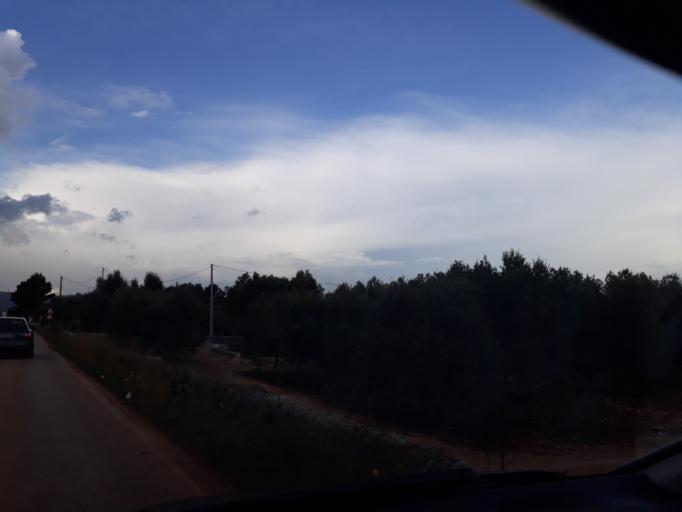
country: IT
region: Apulia
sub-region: Provincia di Brindisi
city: Pezze di Greco
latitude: 40.7988
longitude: 17.4087
